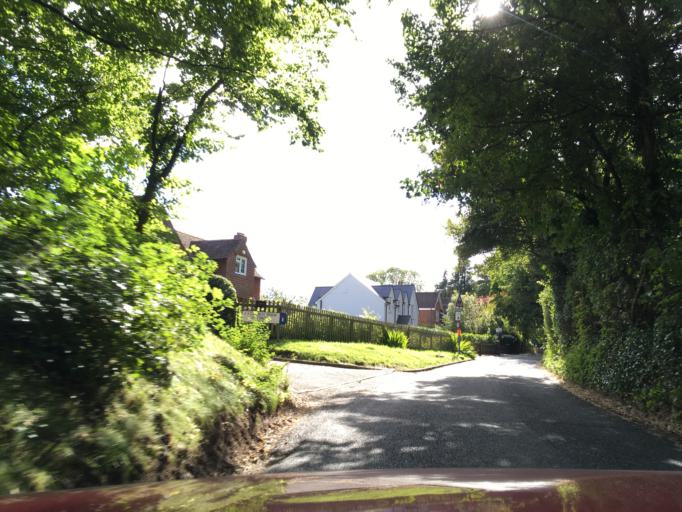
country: GB
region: England
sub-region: Hampshire
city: Winchester
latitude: 51.0796
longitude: -1.3771
